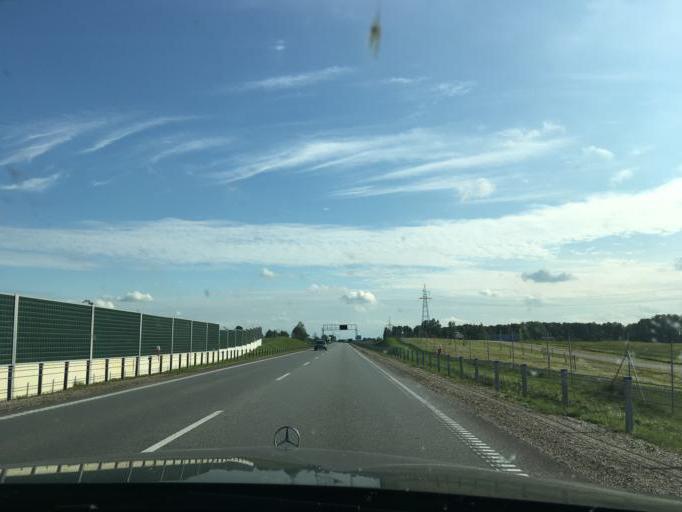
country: PL
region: Podlasie
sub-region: Powiat augustowski
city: Augustow
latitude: 53.8810
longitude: 22.8759
